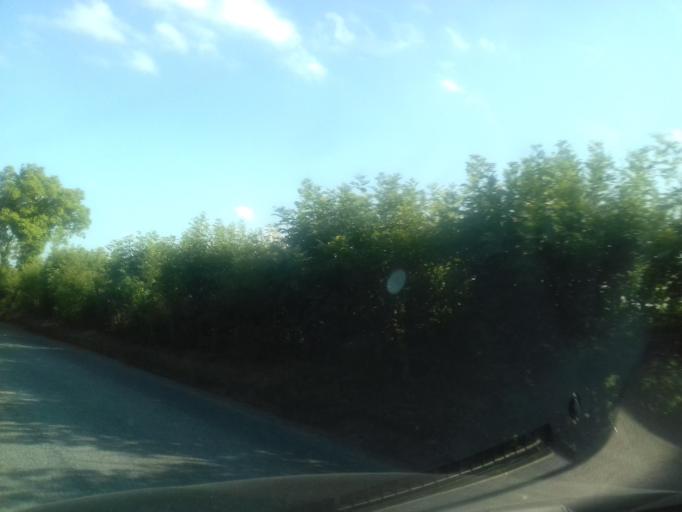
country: IE
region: Leinster
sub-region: Fingal County
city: Blanchardstown
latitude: 53.4411
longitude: -6.3854
